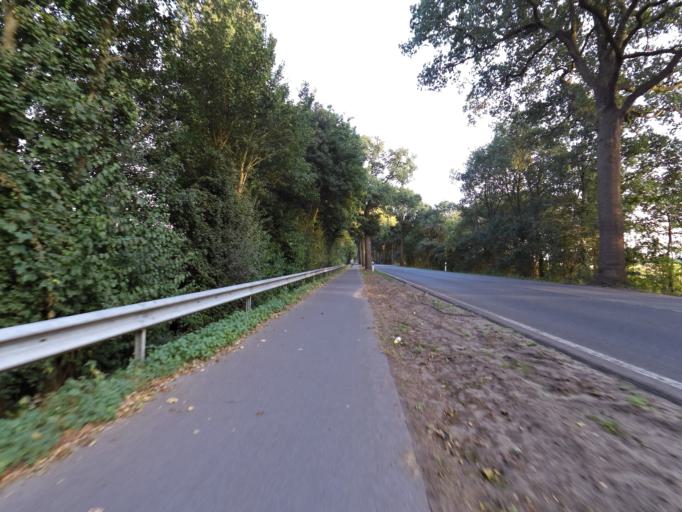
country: NL
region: Gelderland
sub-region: Gemeente Zevenaar
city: Zevenaar
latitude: 51.8990
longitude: 6.1362
